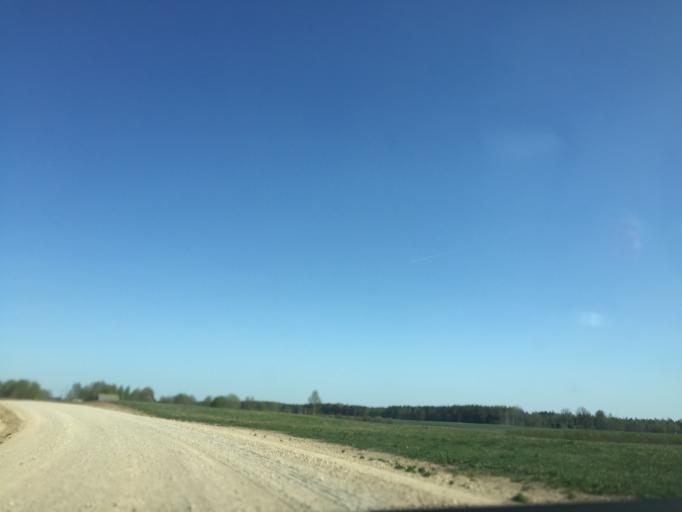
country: LV
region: Skriveri
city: Skriveri
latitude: 56.8330
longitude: 25.2195
